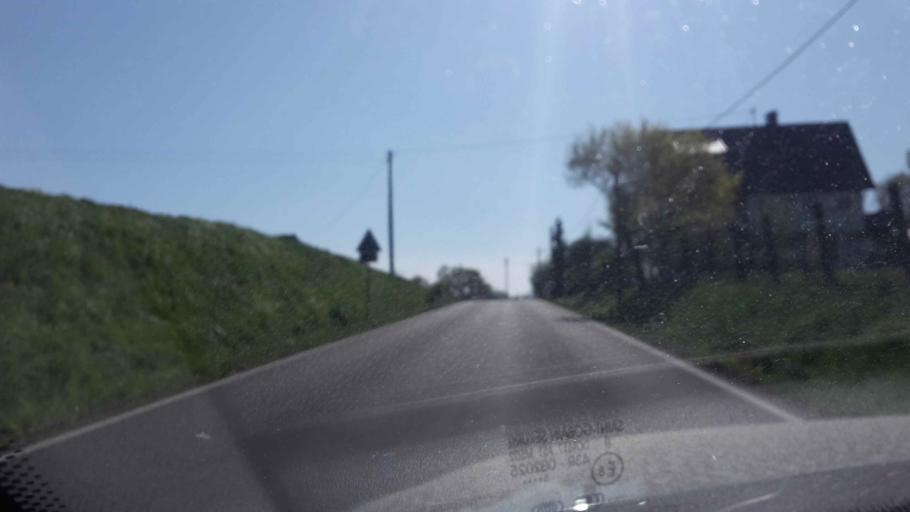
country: DE
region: Rheinland-Pfalz
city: Windhagen
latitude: 50.6786
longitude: 7.3355
